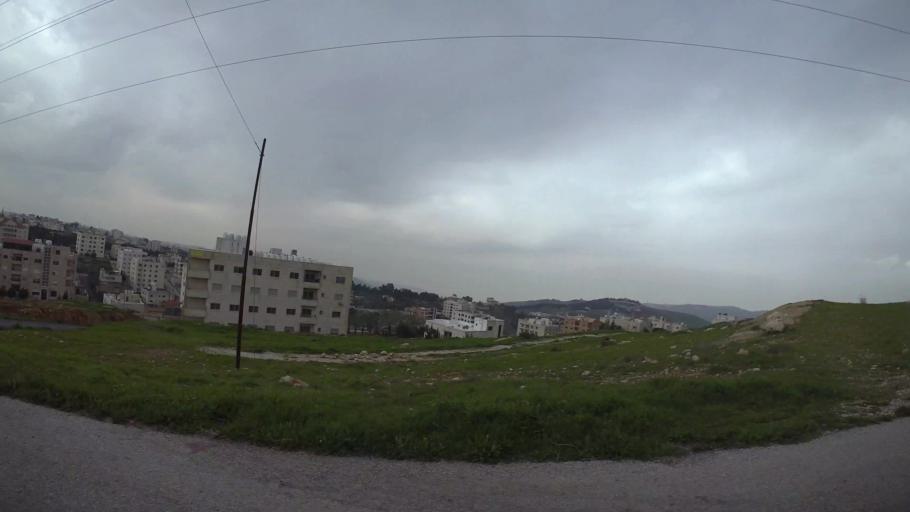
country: JO
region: Amman
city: Umm as Summaq
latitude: 31.9019
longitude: 35.8325
